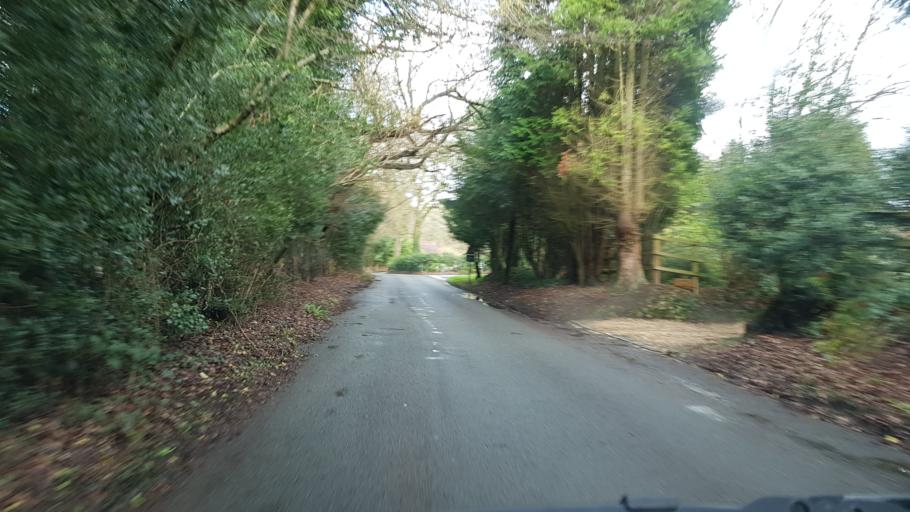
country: GB
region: England
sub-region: Surrey
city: Churt
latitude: 51.1432
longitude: -0.7575
